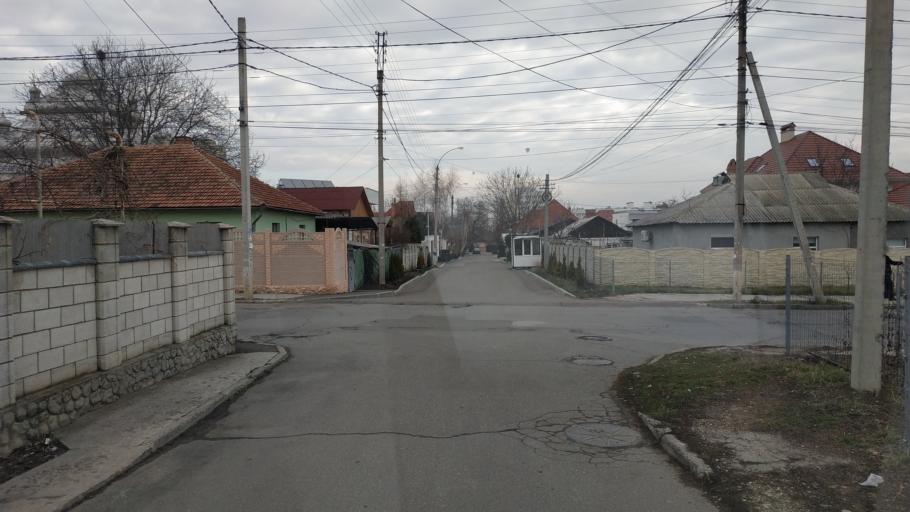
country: MD
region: Chisinau
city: Vatra
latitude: 47.0335
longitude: 28.7848
